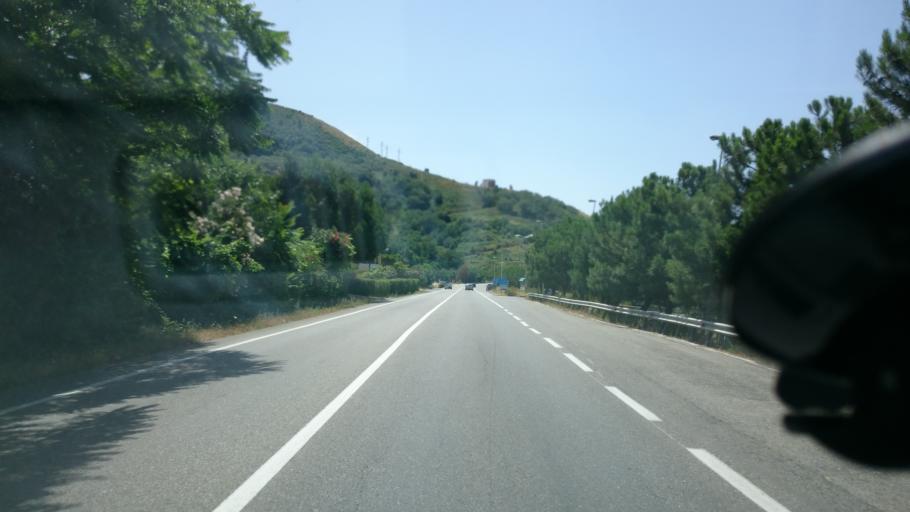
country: IT
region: Calabria
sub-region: Provincia di Cosenza
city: Cittadella del Capo
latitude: 39.5895
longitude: 15.8687
